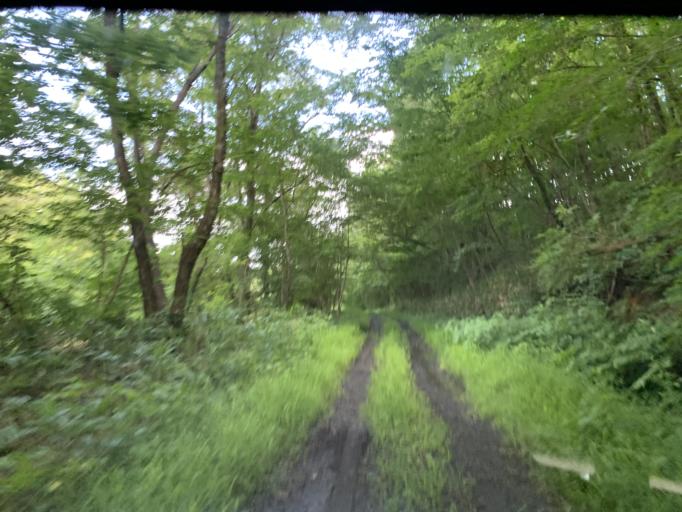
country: JP
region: Iwate
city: Ichinoseki
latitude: 38.9088
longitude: 140.9485
